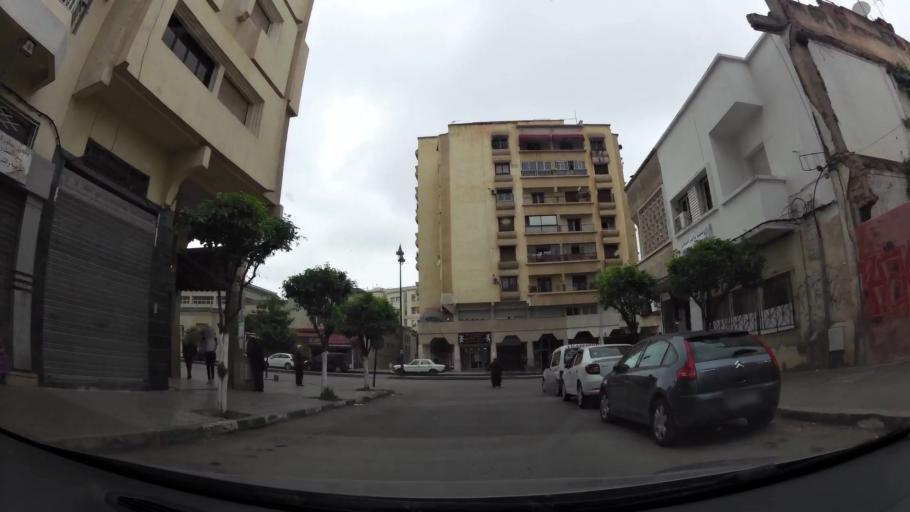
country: MA
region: Fes-Boulemane
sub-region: Fes
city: Fes
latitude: 34.0438
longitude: -5.0054
